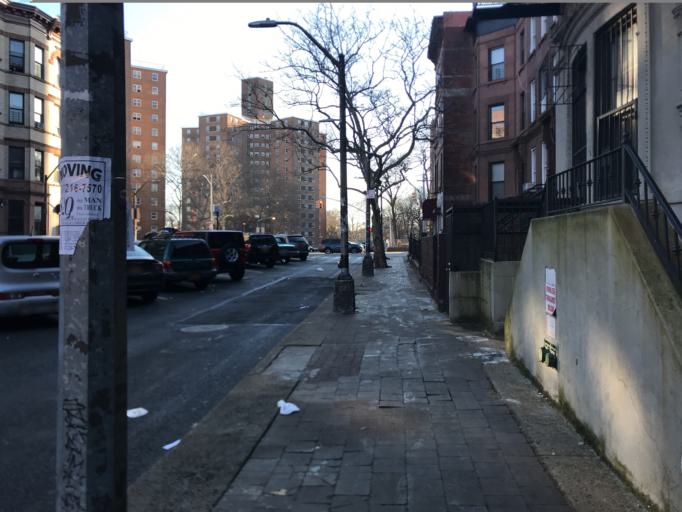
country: US
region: New York
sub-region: Kings County
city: Brooklyn
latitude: 40.6747
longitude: -73.9396
